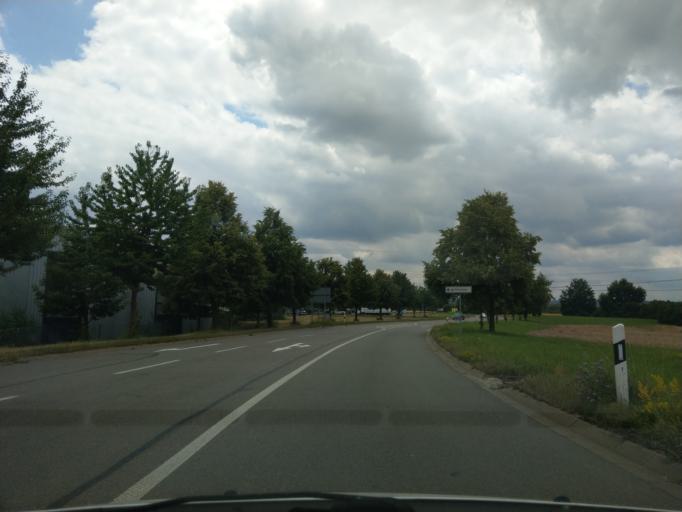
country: DE
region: Baden-Wuerttemberg
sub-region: Regierungsbezirk Stuttgart
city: Ostfildern
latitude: 48.7062
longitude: 9.2490
